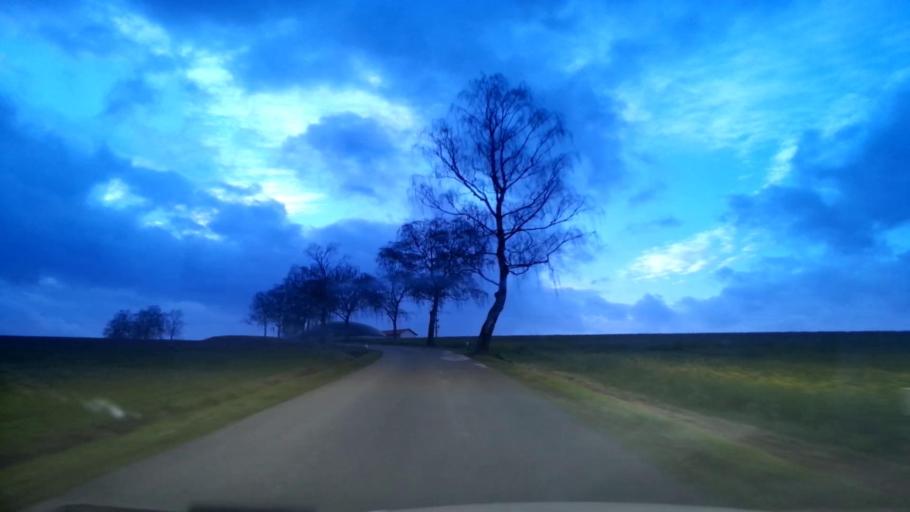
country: DE
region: Bavaria
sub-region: Upper Palatinate
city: Waldershof
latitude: 49.9673
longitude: 12.0893
